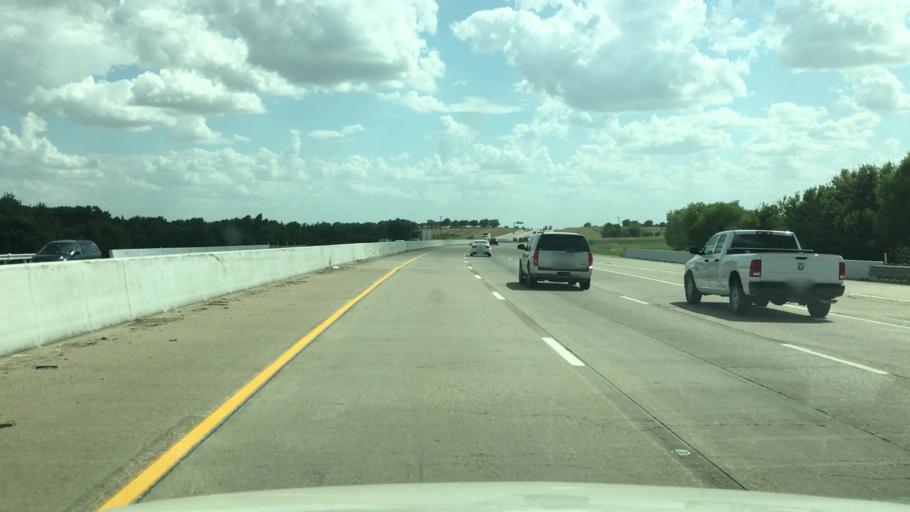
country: US
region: Texas
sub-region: Ellis County
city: Italy
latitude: 32.1739
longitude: -96.9109
